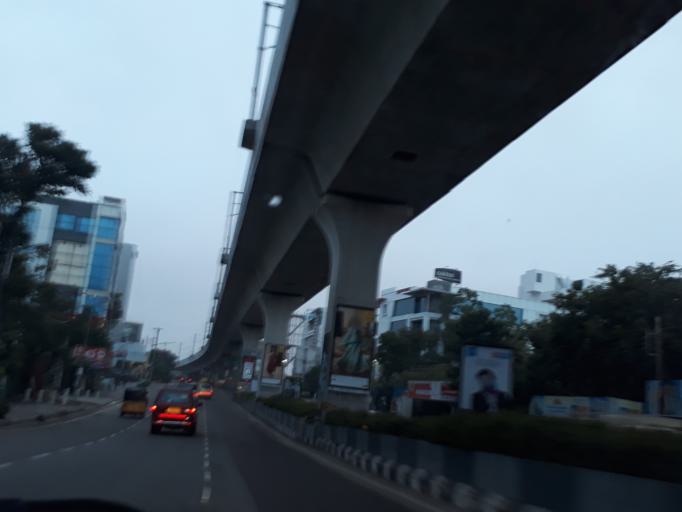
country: IN
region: Telangana
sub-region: Rangareddi
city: Kukatpalli
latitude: 17.4330
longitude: 78.4064
